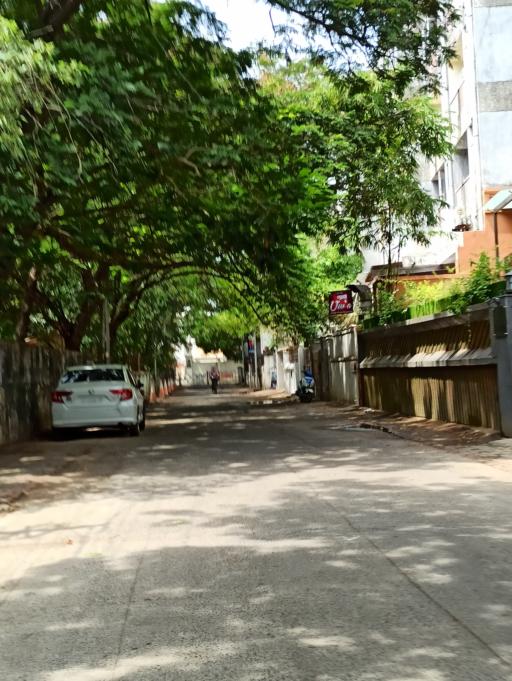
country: IN
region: Tamil Nadu
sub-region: Chennai
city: Chetput
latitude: 13.0701
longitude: 80.2398
